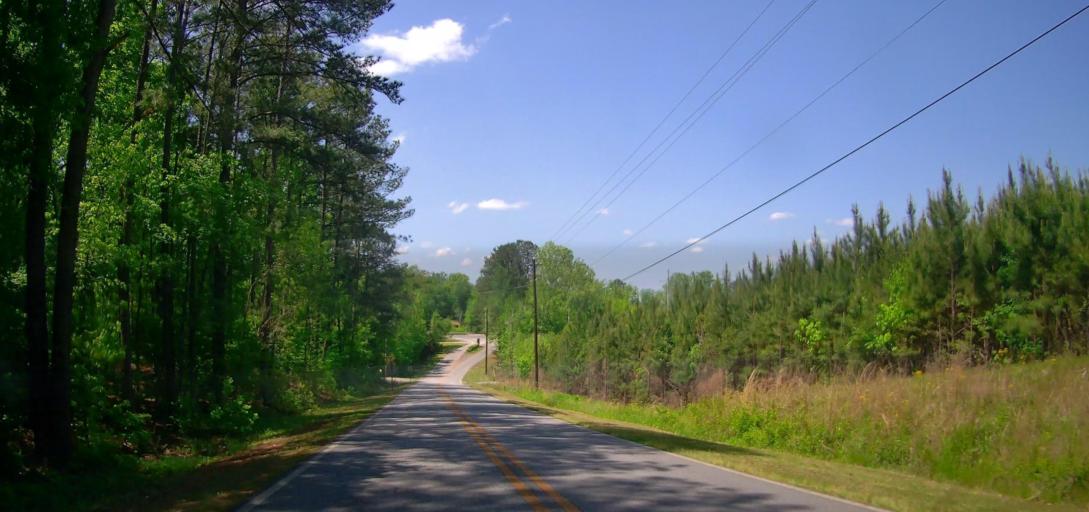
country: US
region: Georgia
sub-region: Jones County
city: Gray
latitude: 32.9451
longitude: -83.5772
